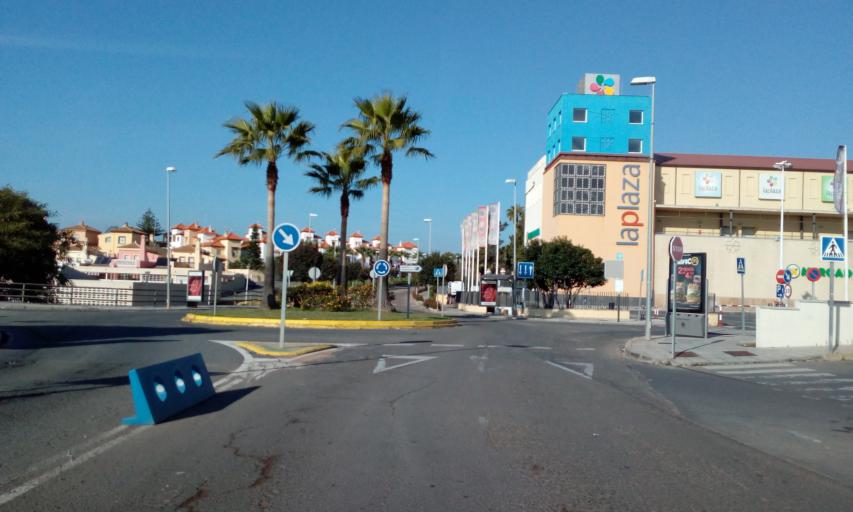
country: ES
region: Andalusia
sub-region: Provincia de Huelva
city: Ayamonte
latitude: 37.2205
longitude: -7.3989
